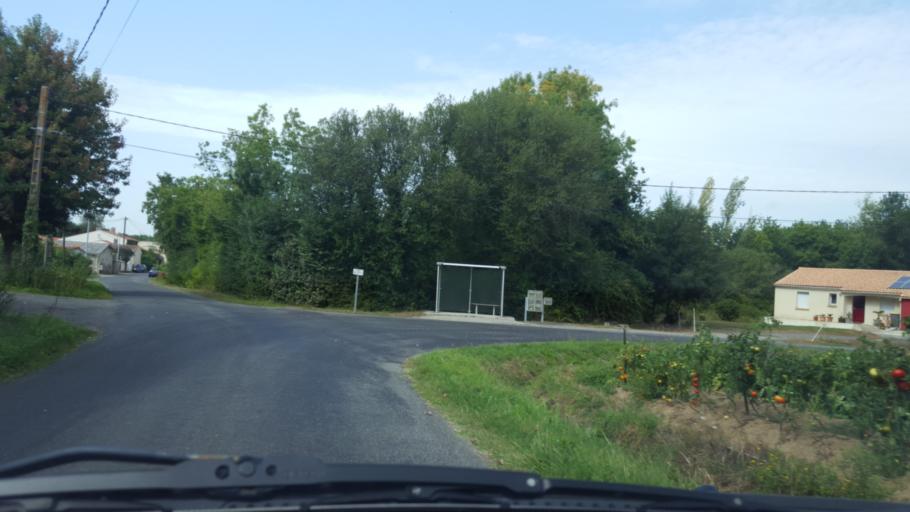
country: FR
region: Pays de la Loire
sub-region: Departement de la Loire-Atlantique
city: La Limouziniere
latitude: 47.0005
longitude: -1.6316
